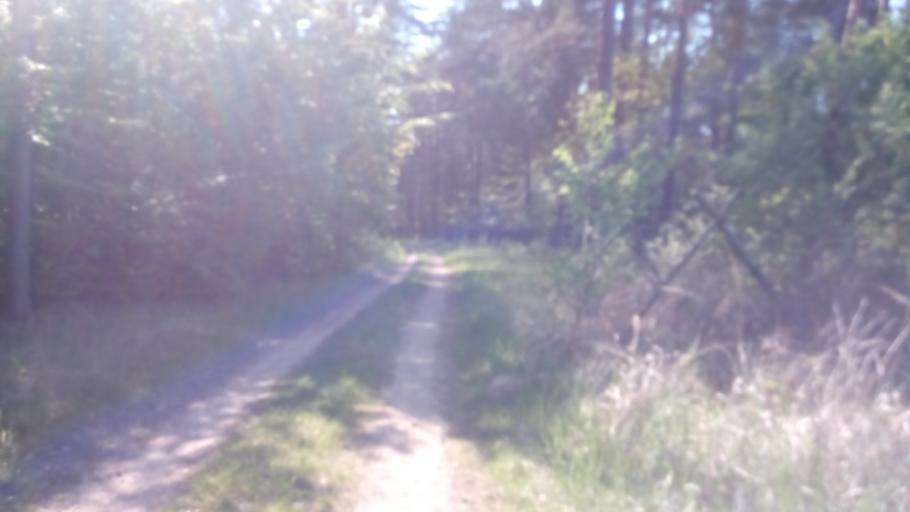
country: PL
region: Opole Voivodeship
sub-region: Powiat opolski
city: Tarnow Opolski
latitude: 50.5845
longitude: 18.0581
